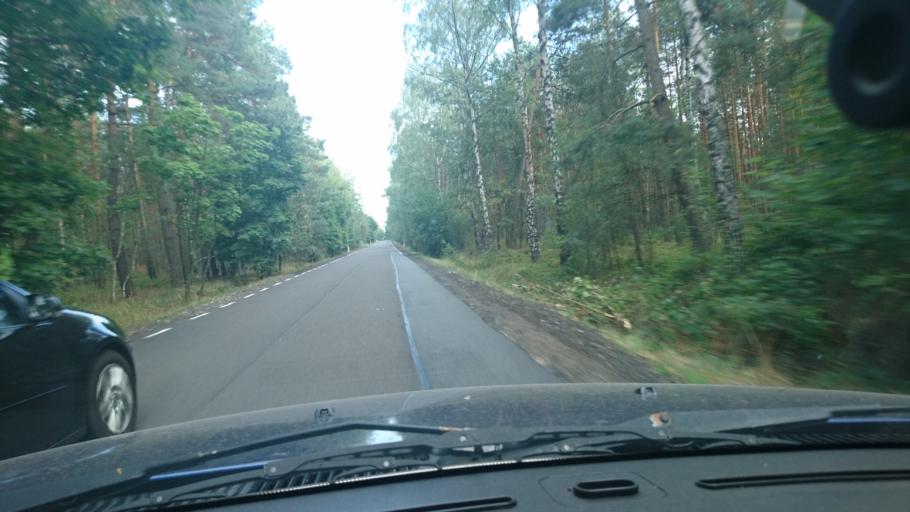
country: PL
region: Greater Poland Voivodeship
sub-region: Powiat ostrowski
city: Jankow Przygodzki
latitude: 51.5318
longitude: 17.7440
